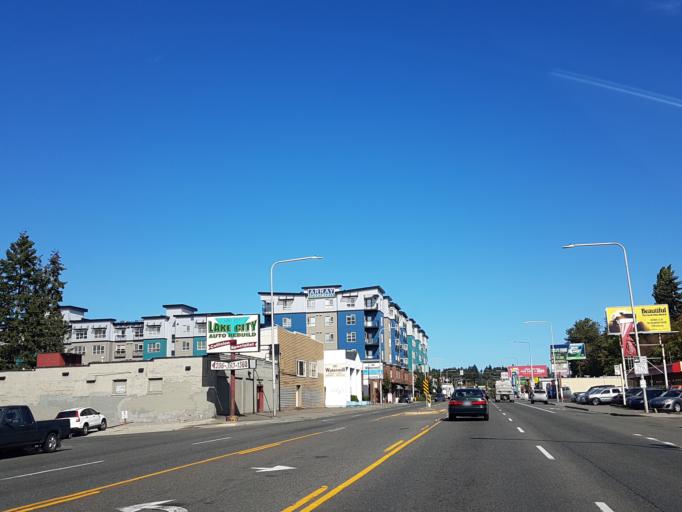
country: US
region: Washington
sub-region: King County
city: Lake Forest Park
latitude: 47.7298
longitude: -122.2923
